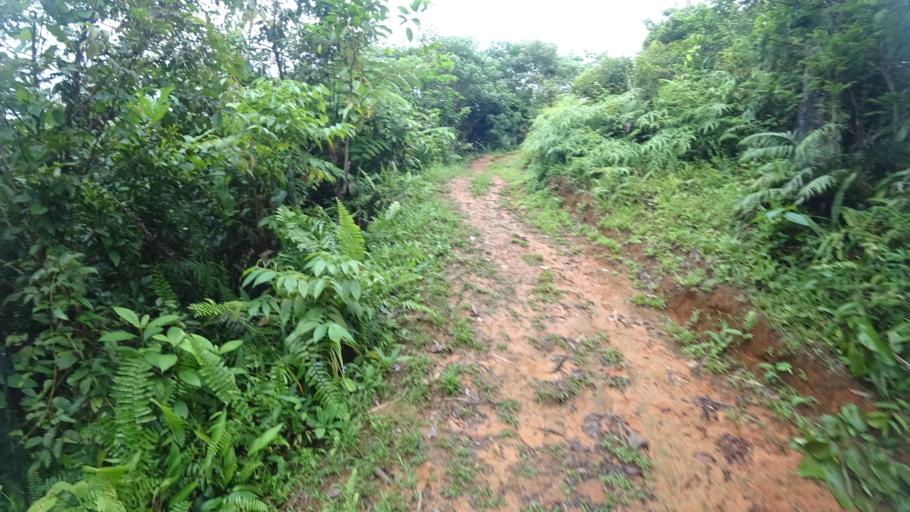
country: PH
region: Eastern Visayas
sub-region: Province of Leyte
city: Bugho
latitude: 10.8279
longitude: 124.8695
